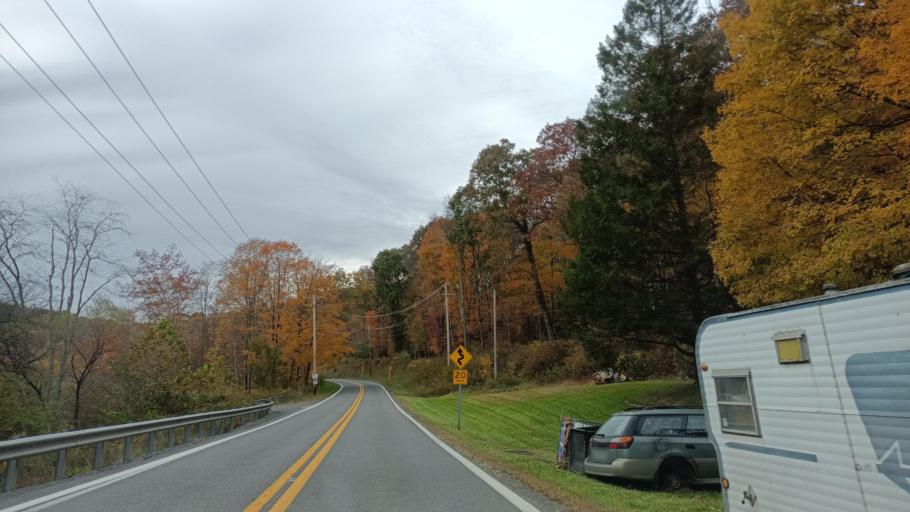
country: US
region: West Virginia
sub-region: Taylor County
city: Grafton
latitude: 39.3338
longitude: -79.8839
